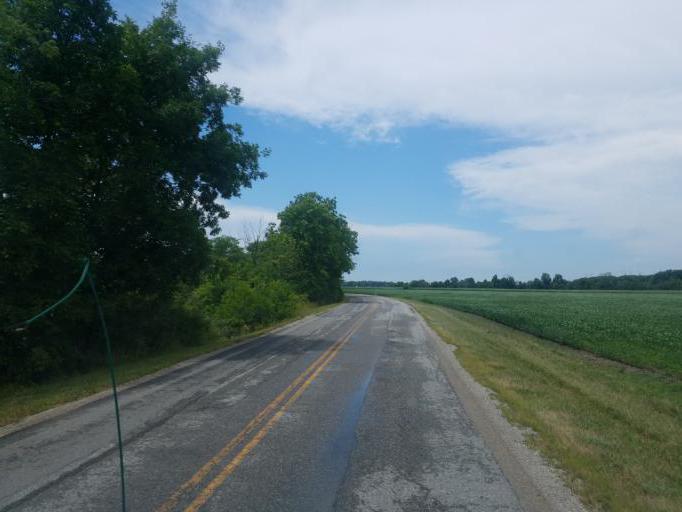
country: US
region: Ohio
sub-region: Paulding County
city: Antwerp
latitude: 41.1980
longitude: -84.7387
